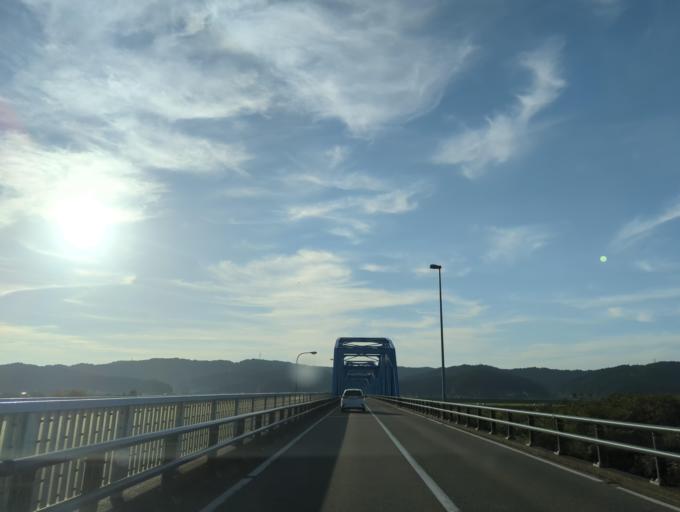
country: JP
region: Niigata
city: Nagaoka
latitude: 37.5535
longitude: 138.8250
